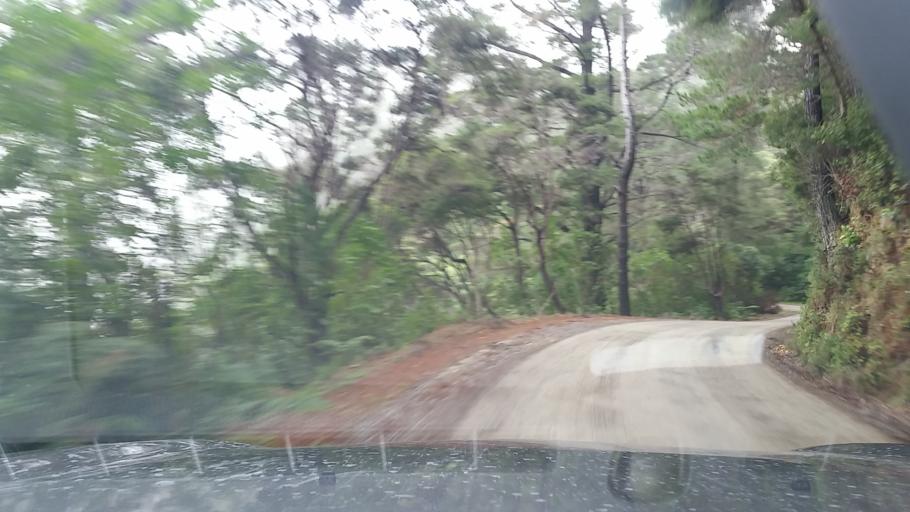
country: NZ
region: Marlborough
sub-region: Marlborough District
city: Picton
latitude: -41.1681
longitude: 174.0186
